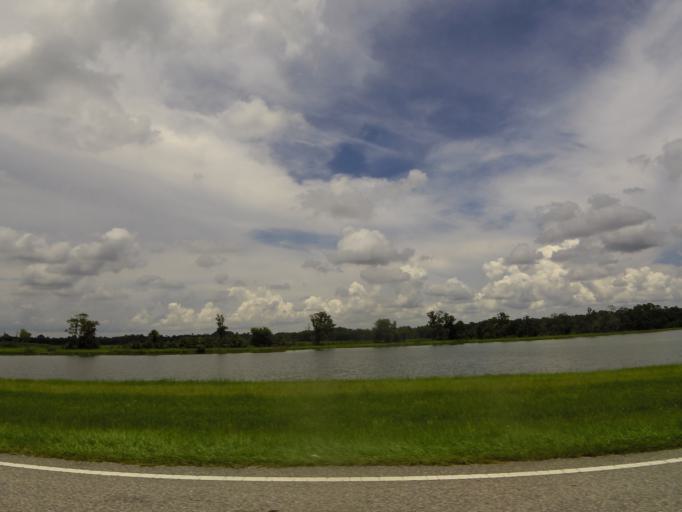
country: US
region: Florida
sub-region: Putnam County
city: East Palatka
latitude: 29.6851
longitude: -81.4761
